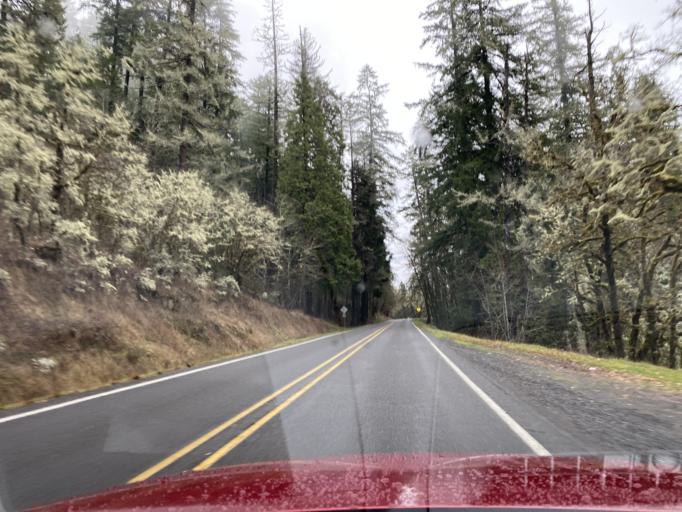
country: US
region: Oregon
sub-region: Lane County
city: Oakridge
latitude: 43.7488
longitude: -122.5120
